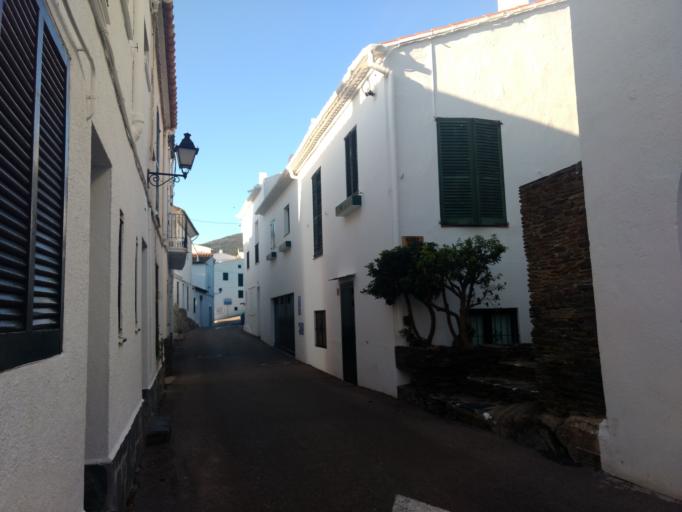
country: ES
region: Catalonia
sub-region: Provincia de Girona
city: Cadaques
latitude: 42.2859
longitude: 3.2763
